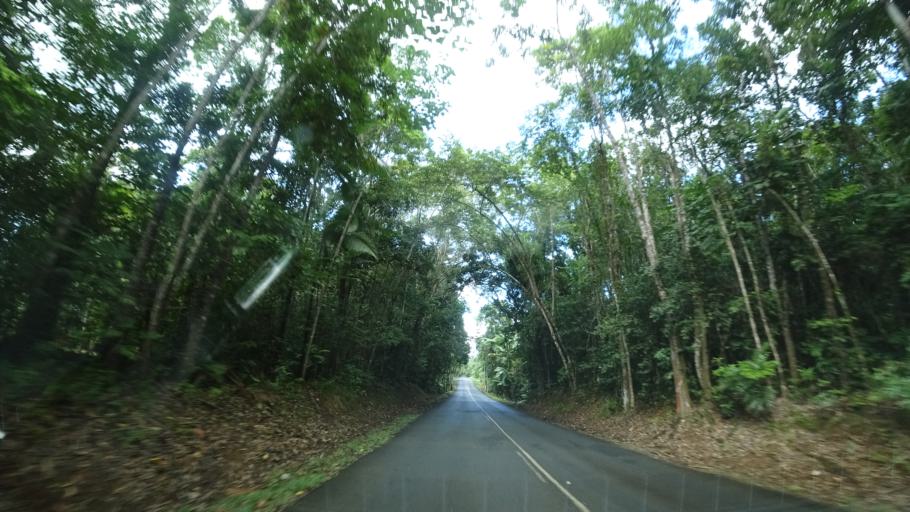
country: AU
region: Queensland
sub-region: Cairns
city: Port Douglas
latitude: -16.1755
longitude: 145.4150
